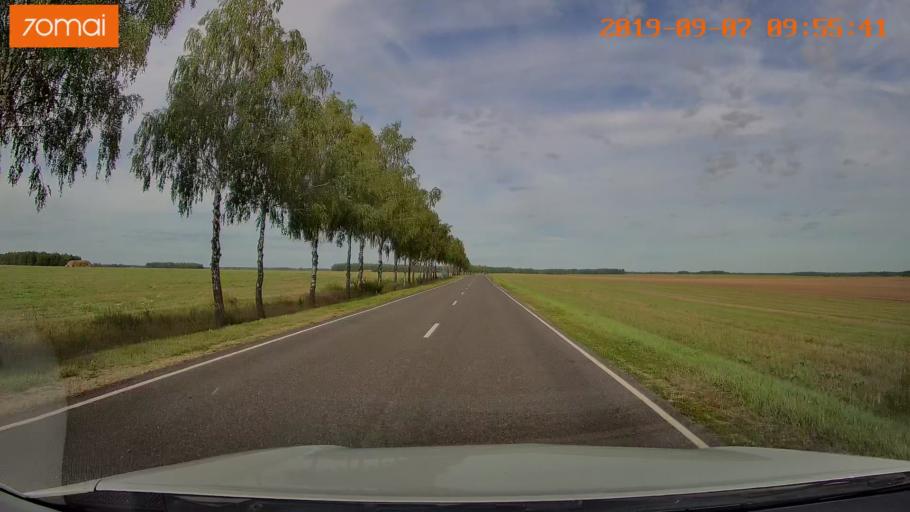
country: BY
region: Grodnenskaya
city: Iwye
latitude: 54.0226
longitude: 25.5618
